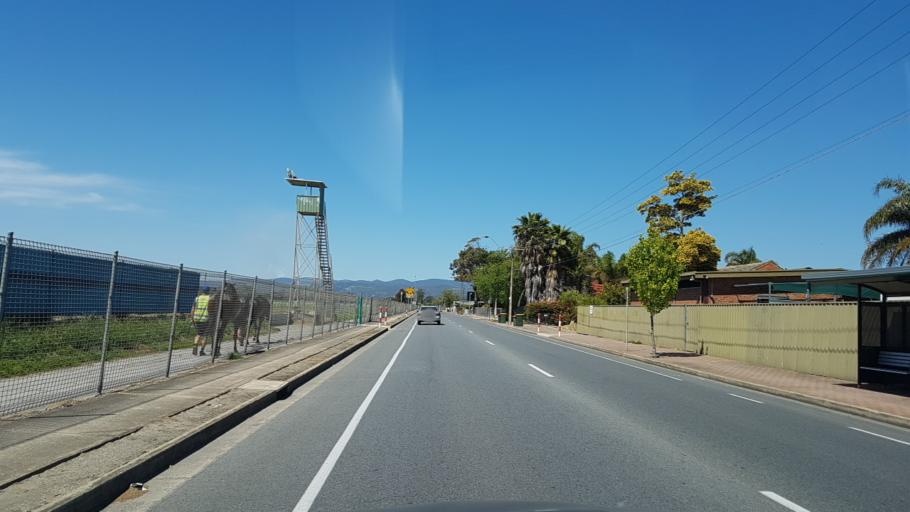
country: AU
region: South Australia
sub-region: Marion
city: Plympton Park
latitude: -34.9813
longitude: 138.5395
